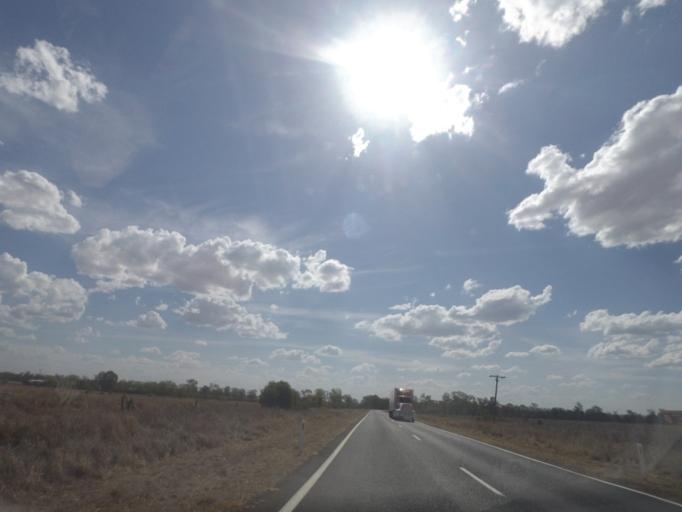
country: AU
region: New South Wales
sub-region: Moree Plains
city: Boggabilla
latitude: -28.4150
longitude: 151.1242
